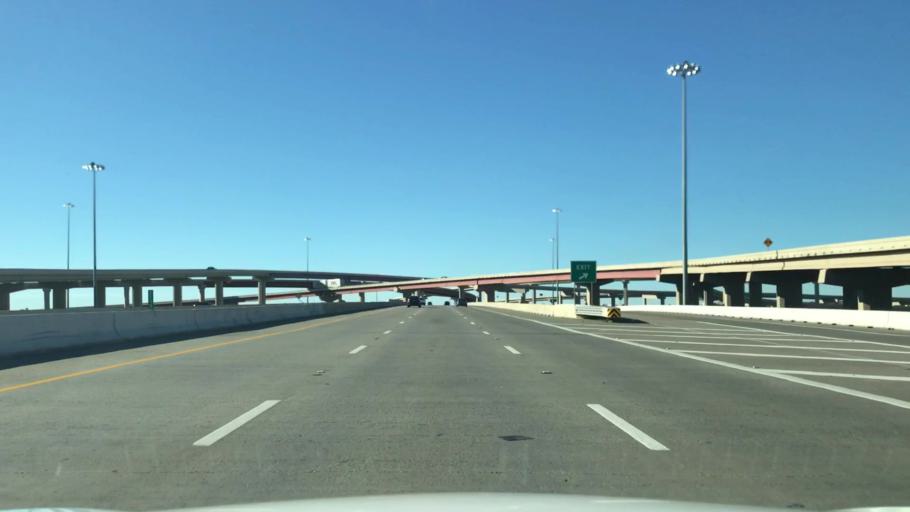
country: US
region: Texas
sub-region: Denton County
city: Lewisville
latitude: 33.0027
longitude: -96.9555
